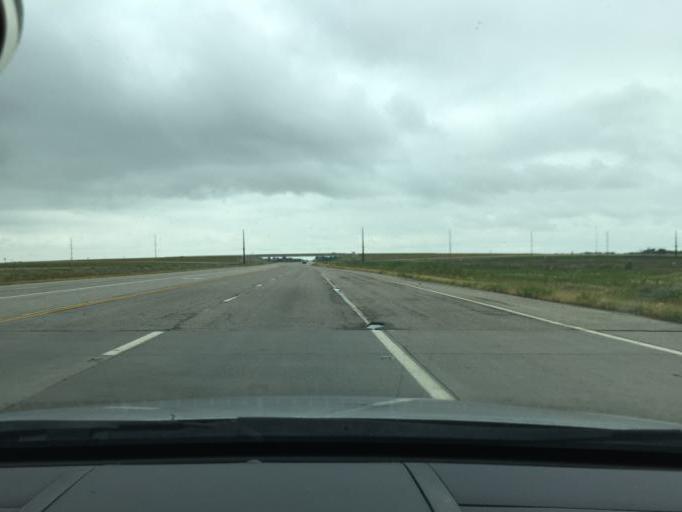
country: US
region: Kansas
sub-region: Reno County
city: Hutchinson
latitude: 38.0337
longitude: -97.8670
